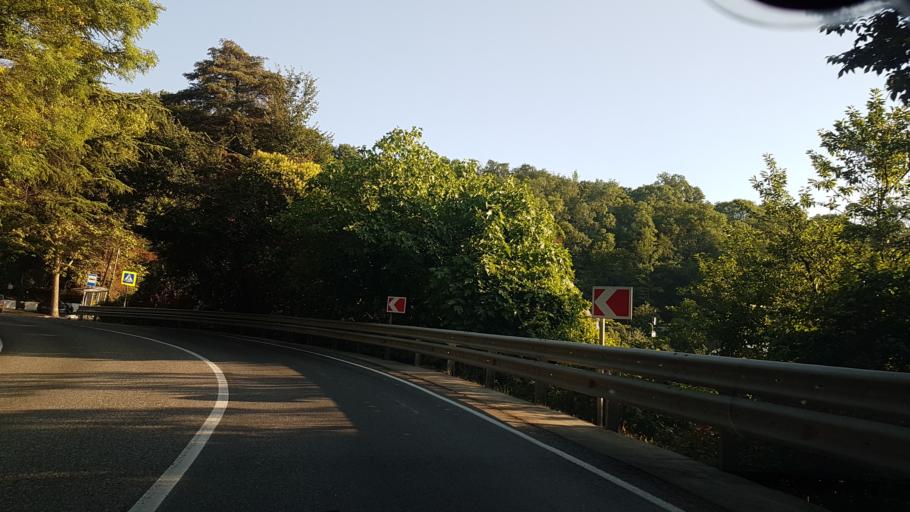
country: RU
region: Krasnodarskiy
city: Dagomys
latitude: 43.6562
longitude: 39.6453
